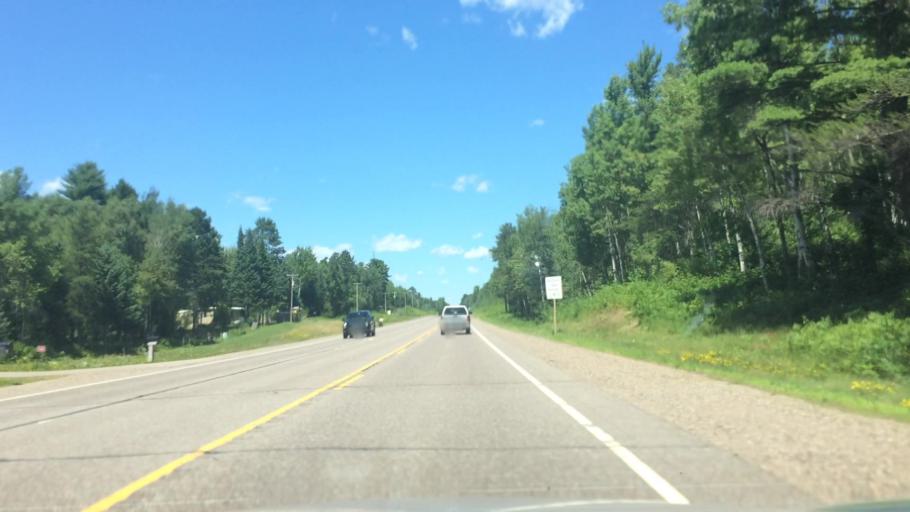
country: US
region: Wisconsin
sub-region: Lincoln County
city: Tomahawk
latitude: 45.6735
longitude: -89.7141
